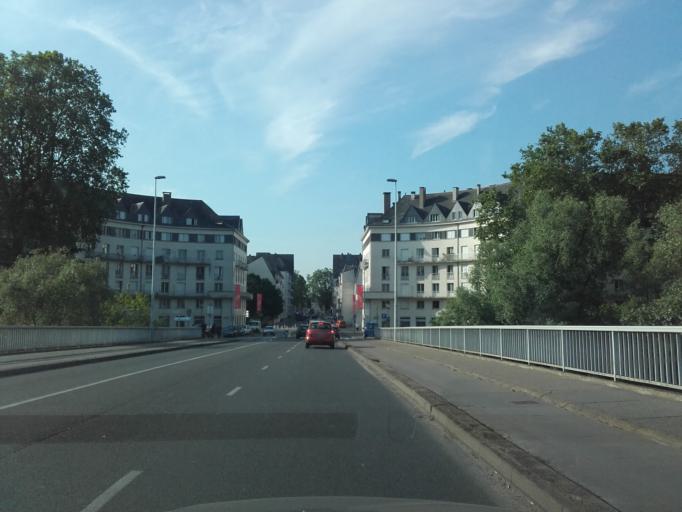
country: FR
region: Centre
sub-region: Departement d'Indre-et-Loire
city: La Riche
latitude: 47.3966
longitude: 0.6767
